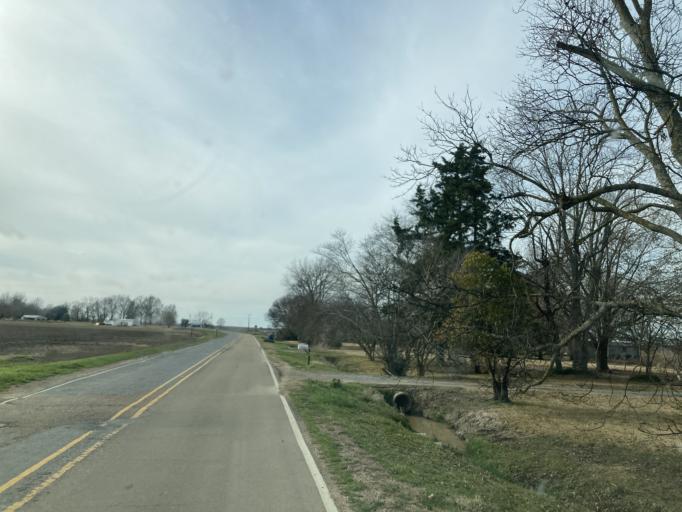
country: US
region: Mississippi
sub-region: Humphreys County
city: Belzoni
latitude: 33.1375
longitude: -90.6079
